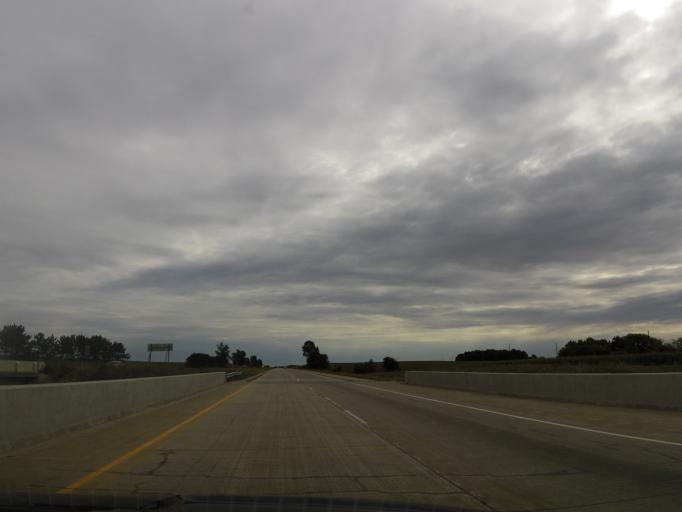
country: US
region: Minnesota
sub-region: Winona County
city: Lewiston
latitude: 43.9343
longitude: -91.8103
